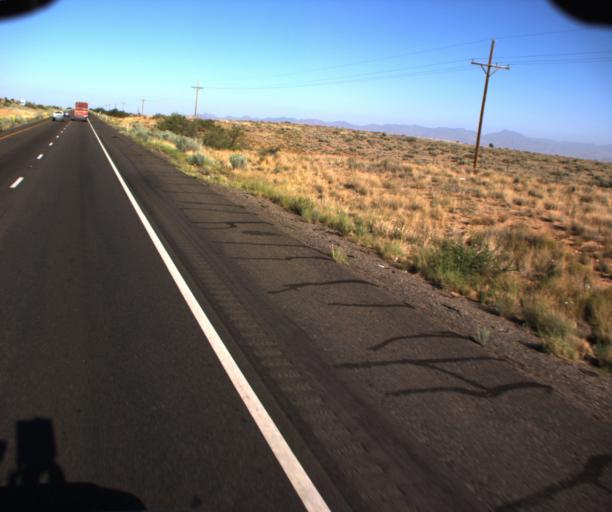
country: US
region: Arizona
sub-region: Mohave County
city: New Kingman-Butler
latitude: 35.1956
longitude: -113.8614
